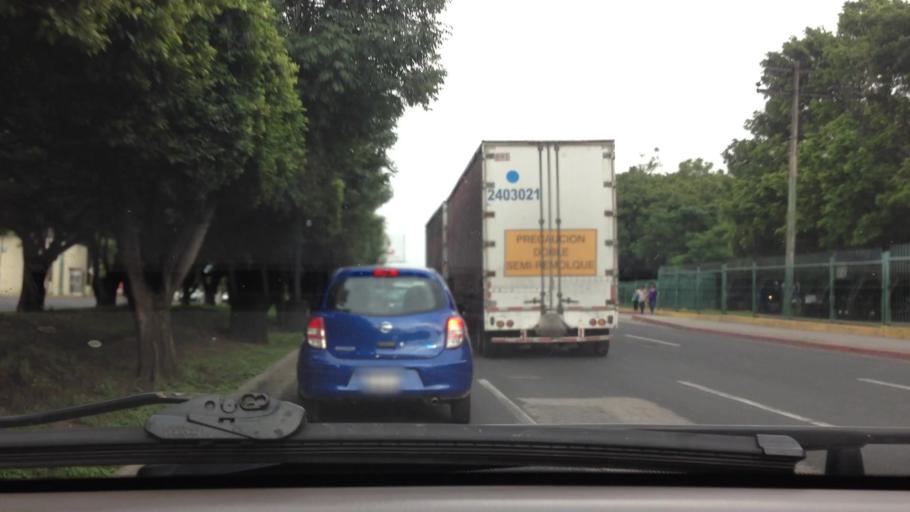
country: MX
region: Morelos
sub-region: Tepoztlan
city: Loma Bonita
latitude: 18.9190
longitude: -99.1907
